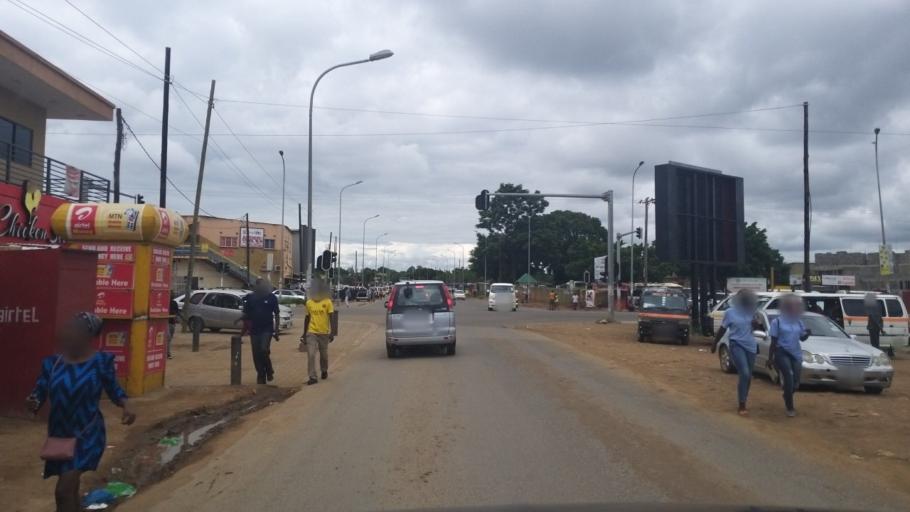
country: ZM
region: Lusaka
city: Lusaka
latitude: -15.4407
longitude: 28.3103
